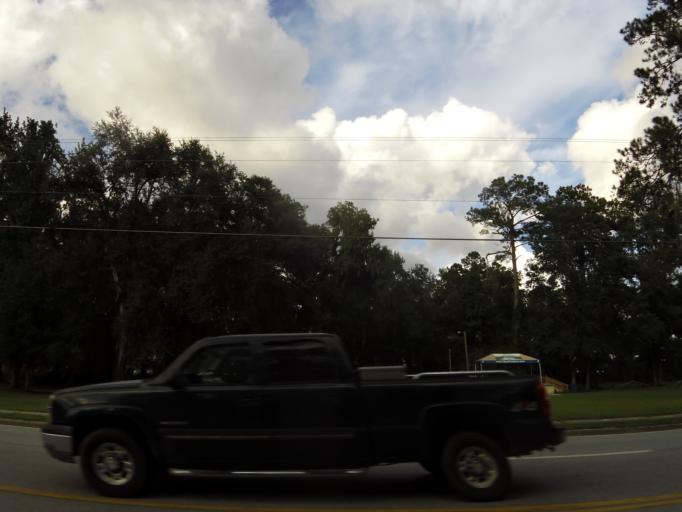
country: US
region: Georgia
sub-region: Liberty County
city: Midway
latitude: 31.7391
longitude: -81.4368
